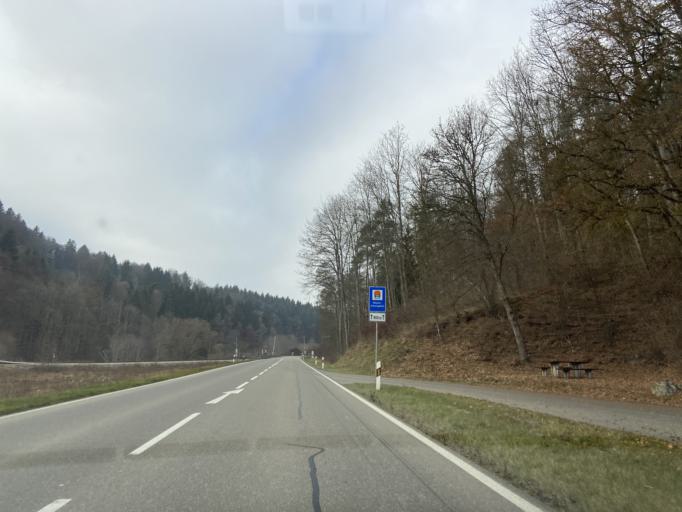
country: DE
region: Baden-Wuerttemberg
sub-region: Tuebingen Region
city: Hettingen
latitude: 48.2337
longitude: 9.2271
